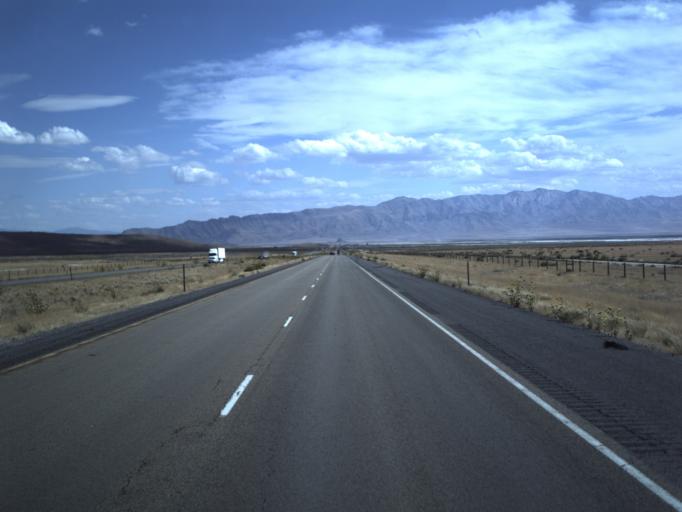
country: US
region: Utah
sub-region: Tooele County
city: Grantsville
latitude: 40.7939
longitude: -112.8386
